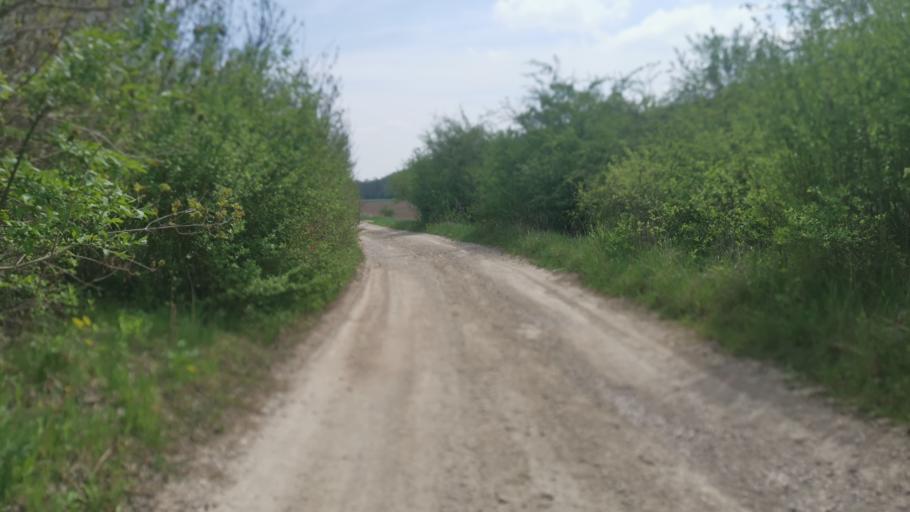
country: SK
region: Trnavsky
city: Smolenice
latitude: 48.5398
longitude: 17.4420
